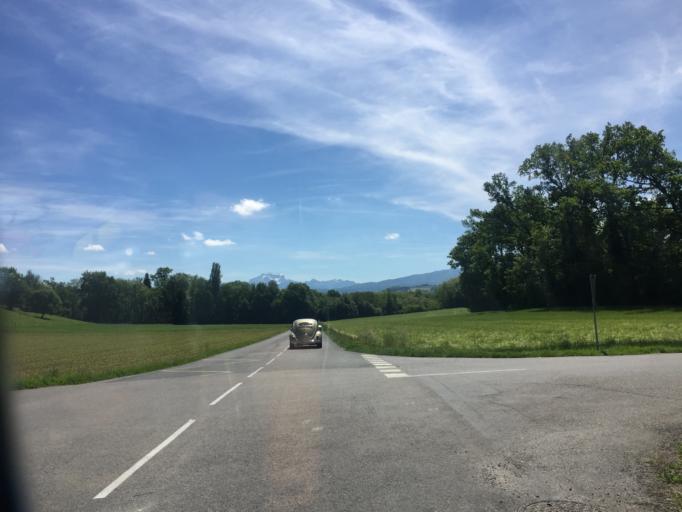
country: FR
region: Rhone-Alpes
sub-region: Departement de la Haute-Savoie
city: Vallieres
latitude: 45.9106
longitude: 5.9538
